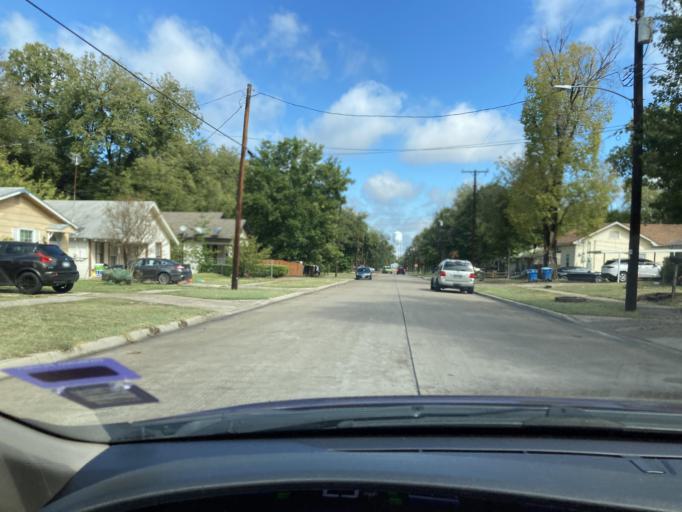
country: US
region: Texas
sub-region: Navarro County
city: Corsicana
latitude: 32.0853
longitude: -96.4804
